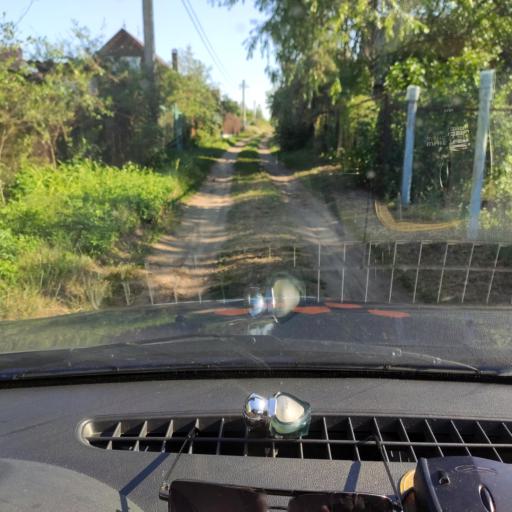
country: RU
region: Voronezj
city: Podgornoye
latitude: 51.8638
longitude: 39.1768
